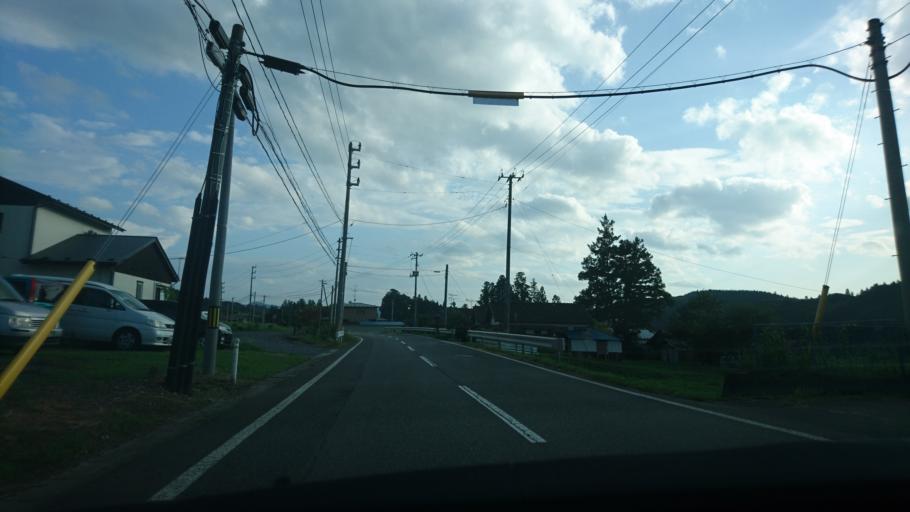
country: JP
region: Iwate
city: Mizusawa
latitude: 39.0301
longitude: 141.2947
